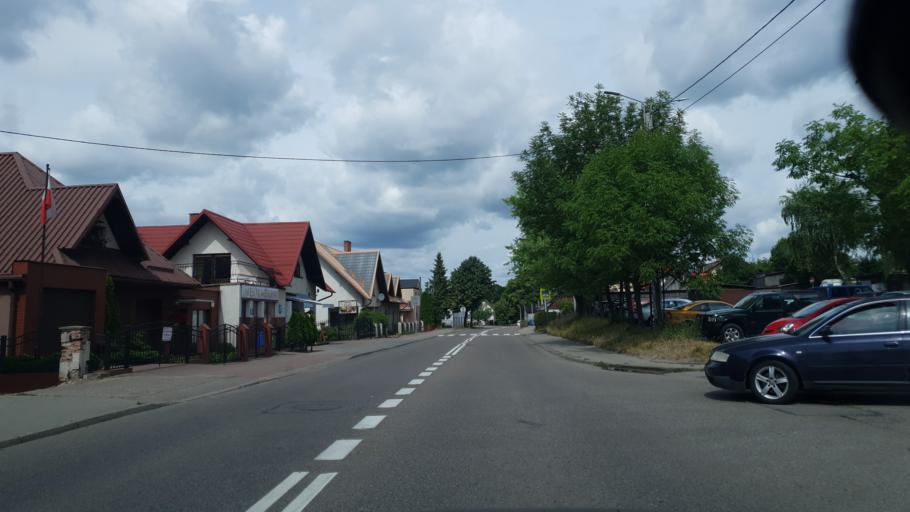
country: PL
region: Pomeranian Voivodeship
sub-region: Powiat kartuski
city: Kartuzy
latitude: 54.3276
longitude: 18.1941
